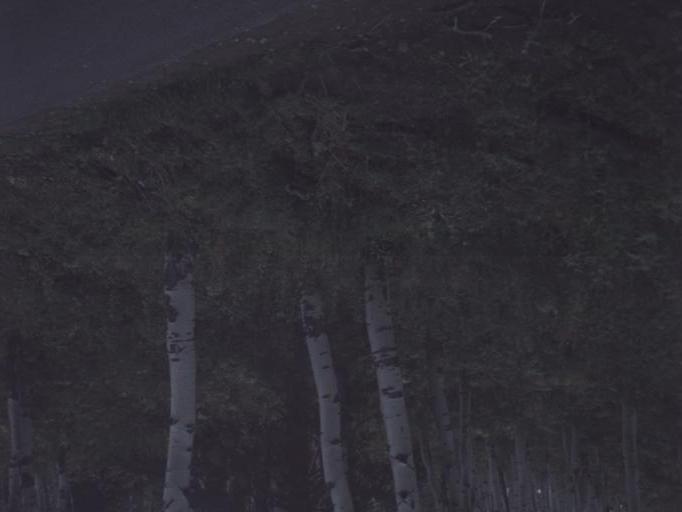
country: US
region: Utah
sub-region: Utah County
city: Lindon
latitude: 40.4225
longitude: -111.6047
